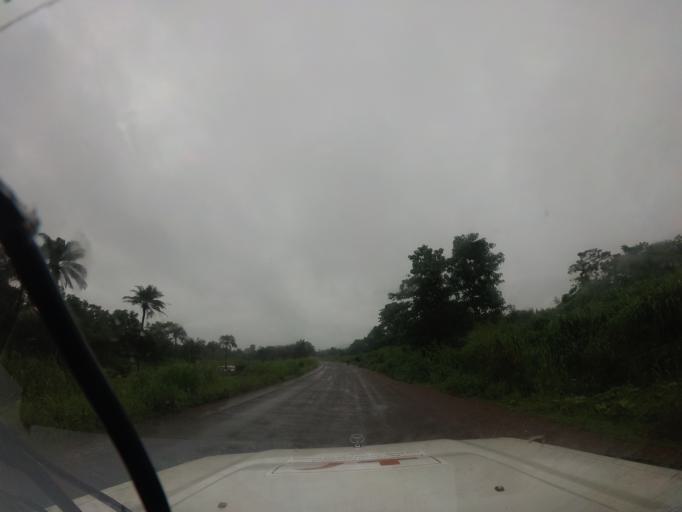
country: SL
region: Northern Province
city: Binkolo
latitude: 8.9268
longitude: -12.0139
